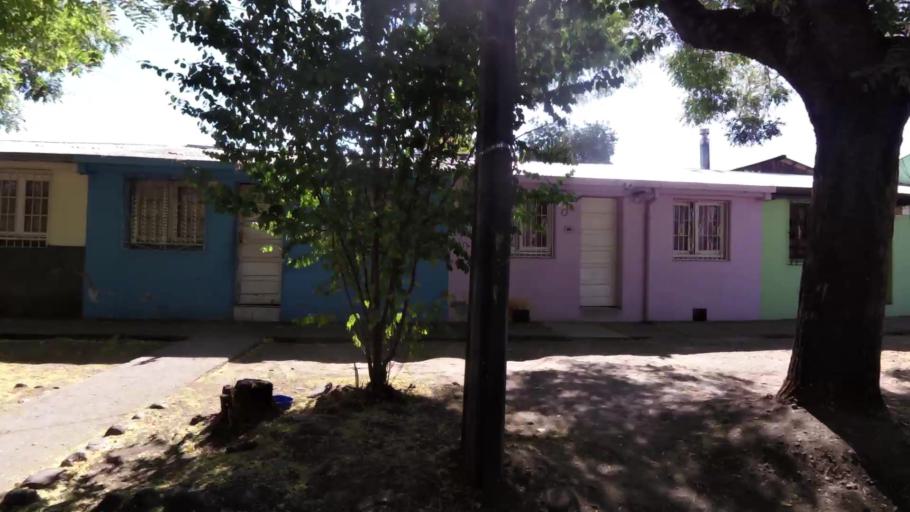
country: CL
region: Maule
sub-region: Provincia de Talca
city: Talca
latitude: -35.4327
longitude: -71.6618
